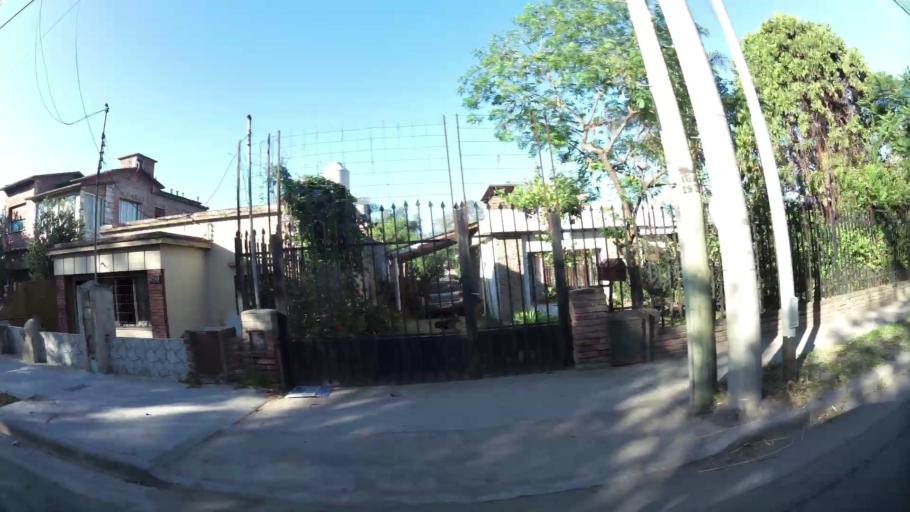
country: AR
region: Cordoba
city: Villa Allende
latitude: -31.3421
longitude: -64.2501
